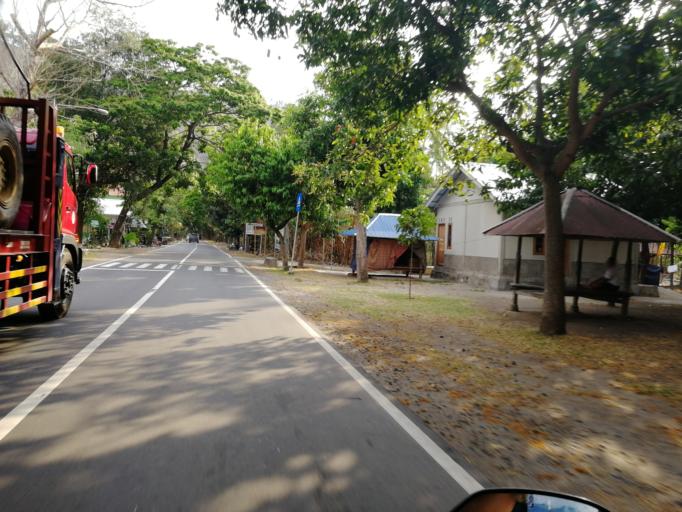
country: ID
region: West Nusa Tenggara
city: Karangsubagan
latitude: -8.4417
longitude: 116.0427
